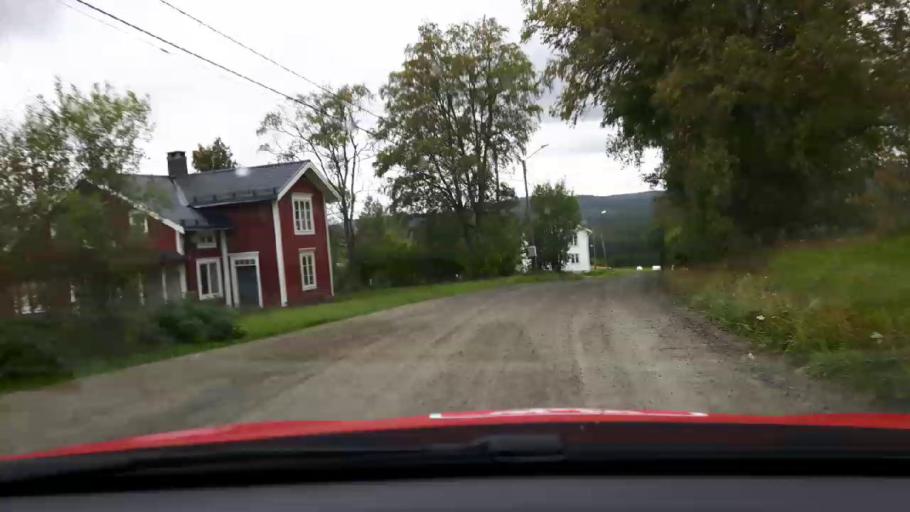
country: SE
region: Jaemtland
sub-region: Bergs Kommun
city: Hoverberg
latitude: 62.8533
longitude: 14.3386
